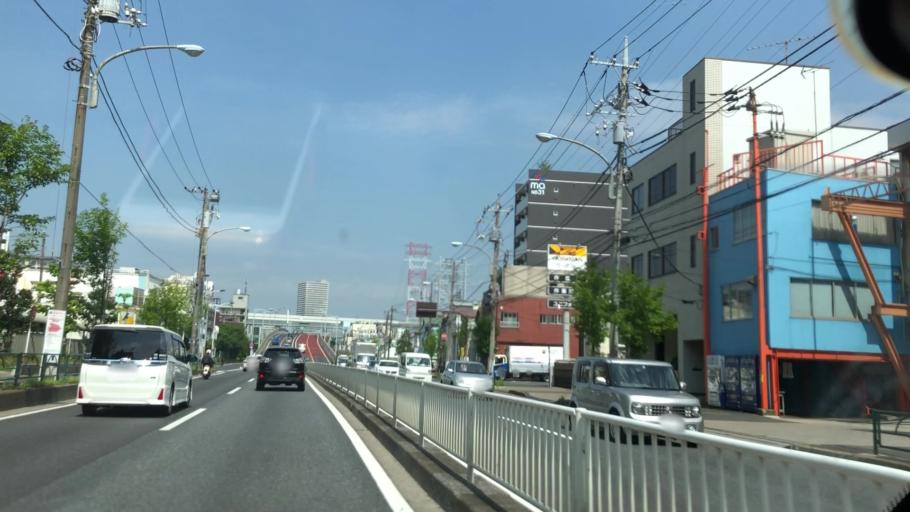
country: JP
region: Tokyo
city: Urayasu
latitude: 35.6868
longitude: 139.8632
